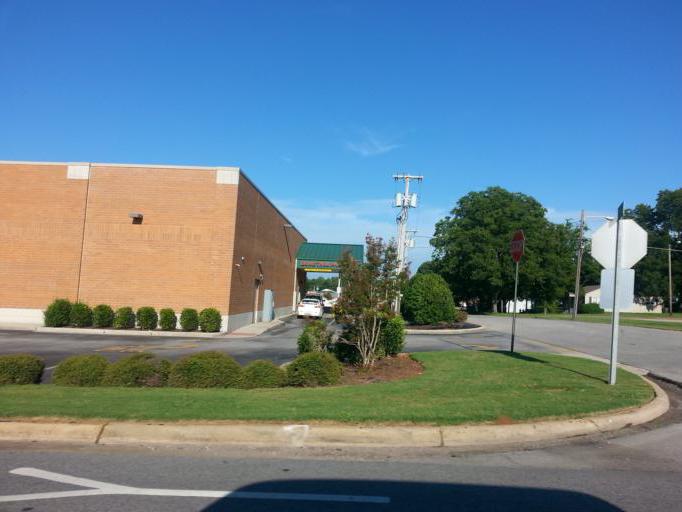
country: US
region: Alabama
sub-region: Colbert County
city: Muscle Shoals
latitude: 34.7439
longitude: -87.6676
